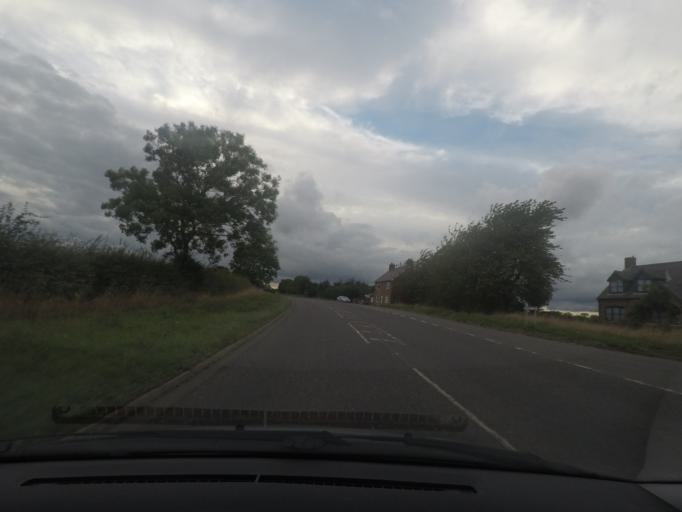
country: GB
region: England
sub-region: Lincolnshire
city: Burwell
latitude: 53.2693
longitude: 0.0762
